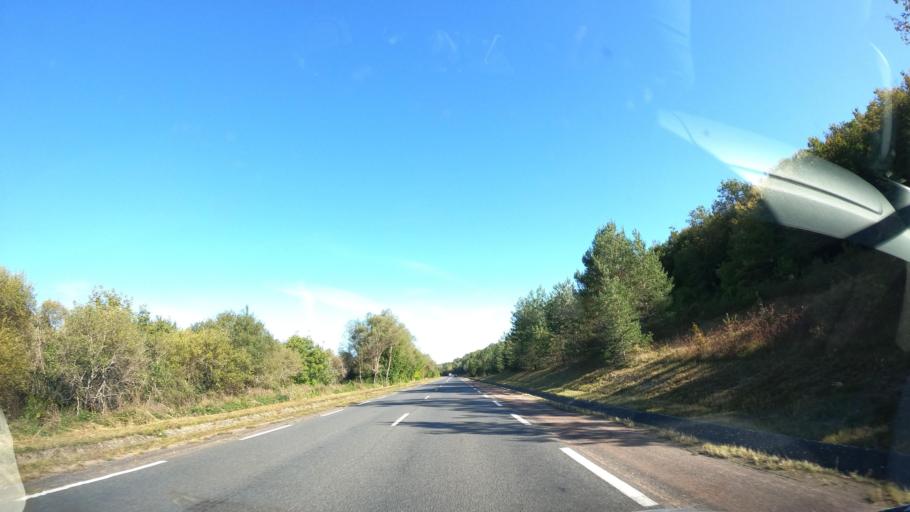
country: FR
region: Aquitaine
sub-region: Departement de la Dordogne
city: Vergt
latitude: 44.9905
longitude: 0.6043
